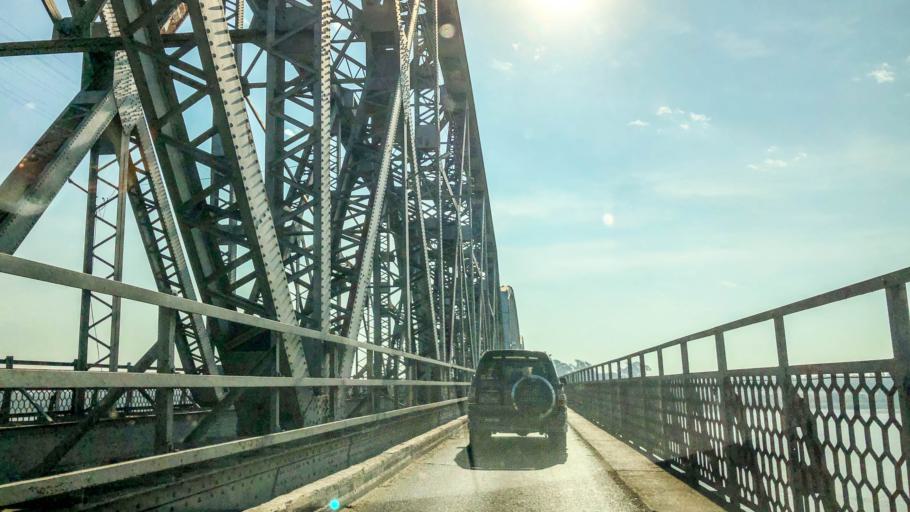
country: MM
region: Sagain
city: Sagaing
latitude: 21.8729
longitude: 95.9907
